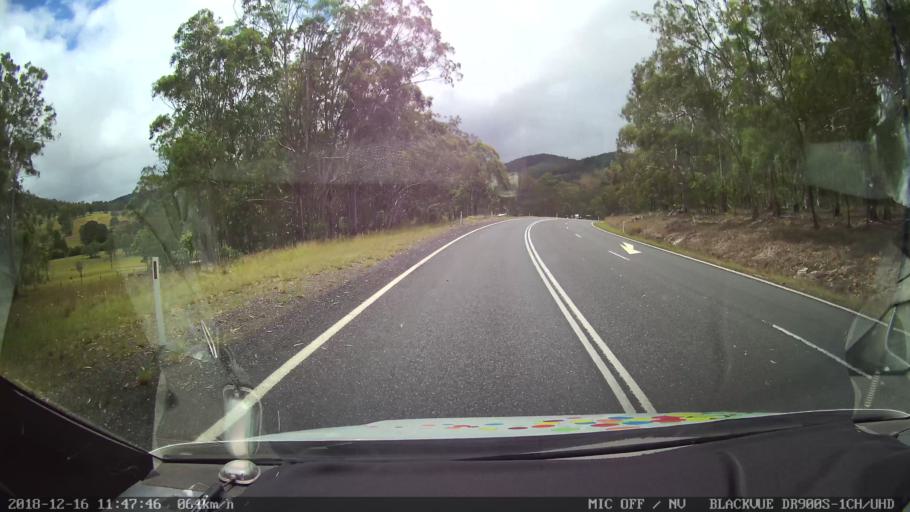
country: AU
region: New South Wales
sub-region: Tenterfield Municipality
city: Carrolls Creek
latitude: -28.9201
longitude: 152.2413
